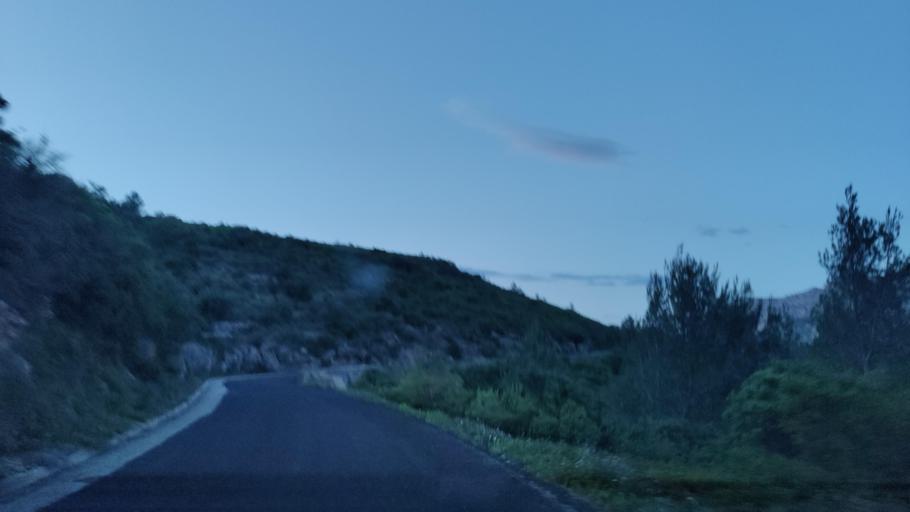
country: FR
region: Languedoc-Roussillon
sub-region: Departement des Pyrenees-Orientales
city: Estagel
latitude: 42.8547
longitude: 2.7686
